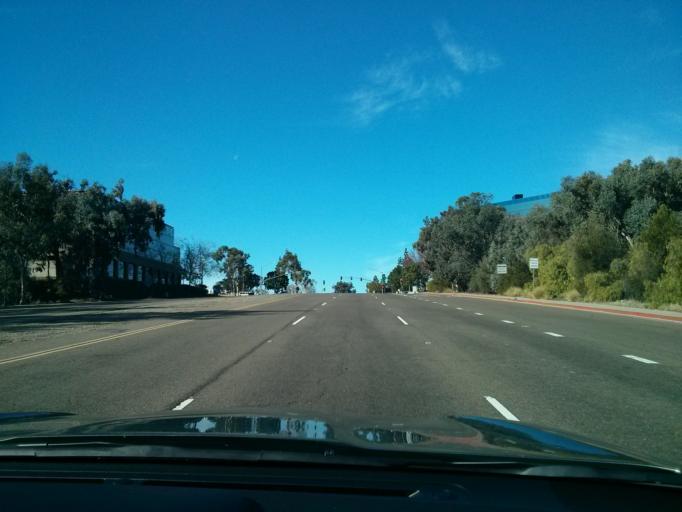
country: US
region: California
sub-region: San Diego County
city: San Diego
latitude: 32.8224
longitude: -117.1253
